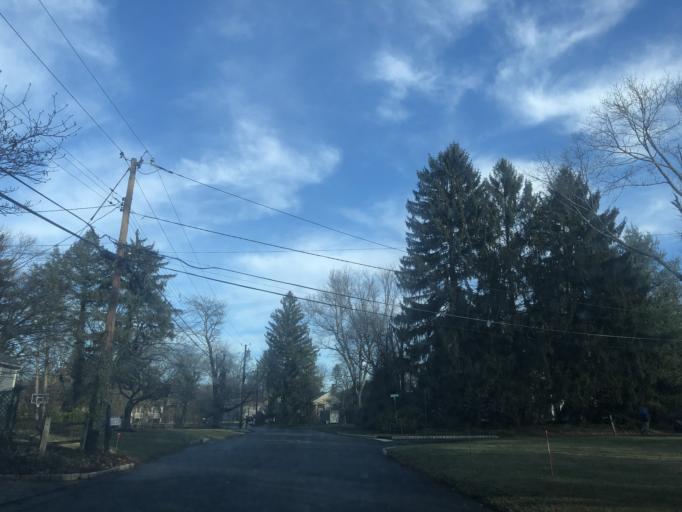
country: US
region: New Jersey
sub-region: Somerset County
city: Kingston
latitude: 40.3685
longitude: -74.6279
